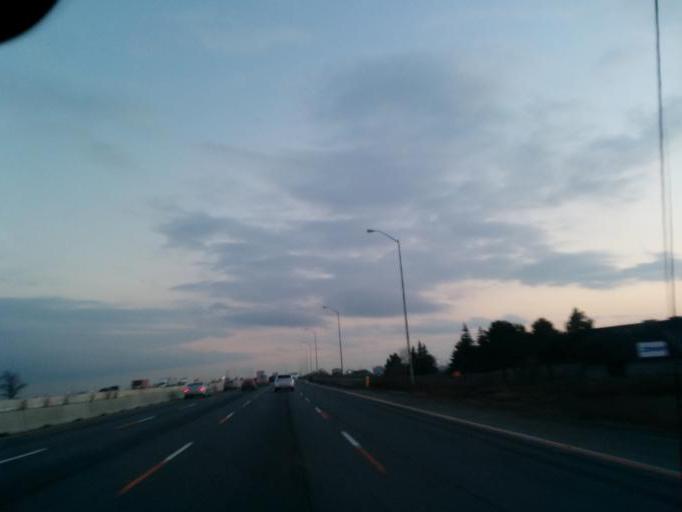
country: CA
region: Ontario
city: Etobicoke
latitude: 43.7118
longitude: -79.6165
